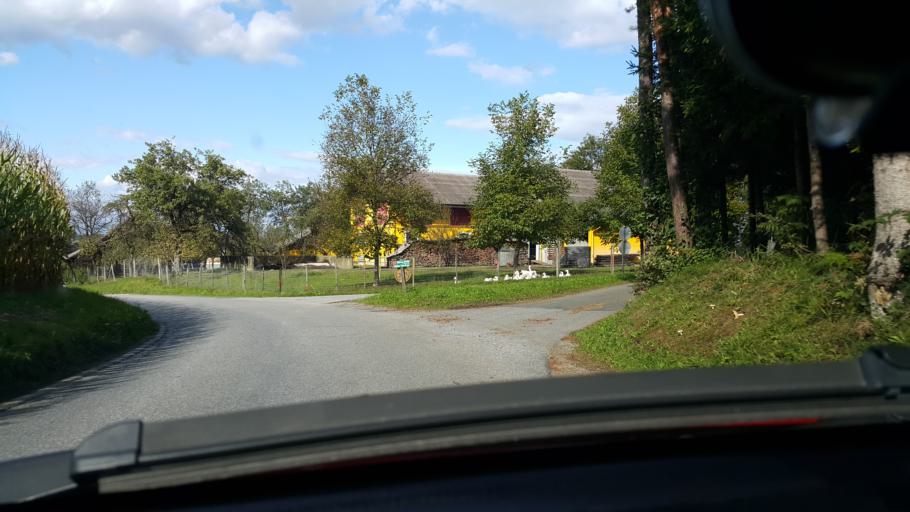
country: AT
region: Styria
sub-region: Politischer Bezirk Deutschlandsberg
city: Sankt Martin im Sulmtal
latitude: 46.7440
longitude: 15.2858
